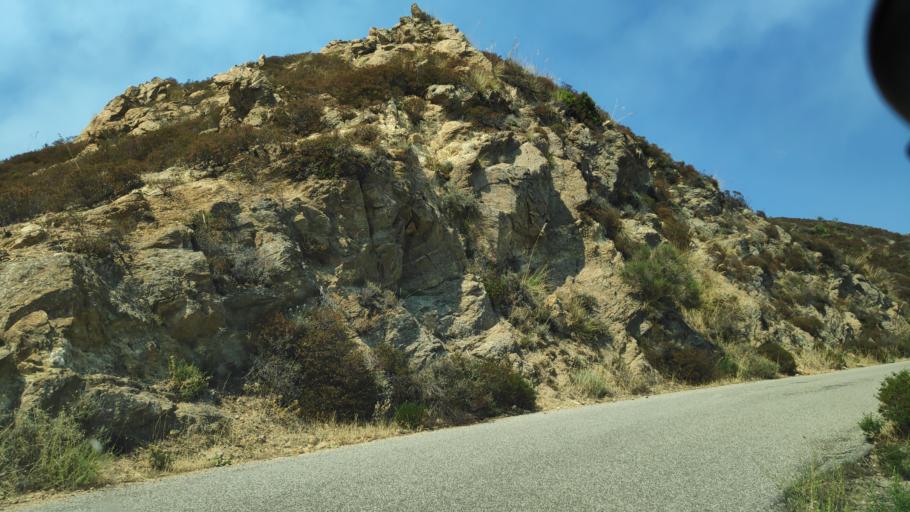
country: IT
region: Calabria
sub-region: Provincia di Reggio Calabria
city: Bova
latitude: 38.0028
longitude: 15.9283
